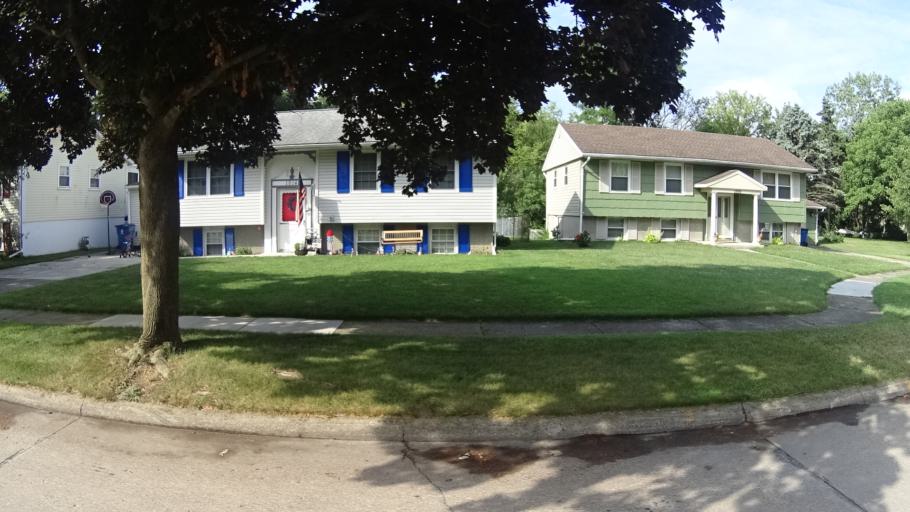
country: US
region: Ohio
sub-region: Erie County
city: Sandusky
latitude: 41.4378
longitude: -82.6784
